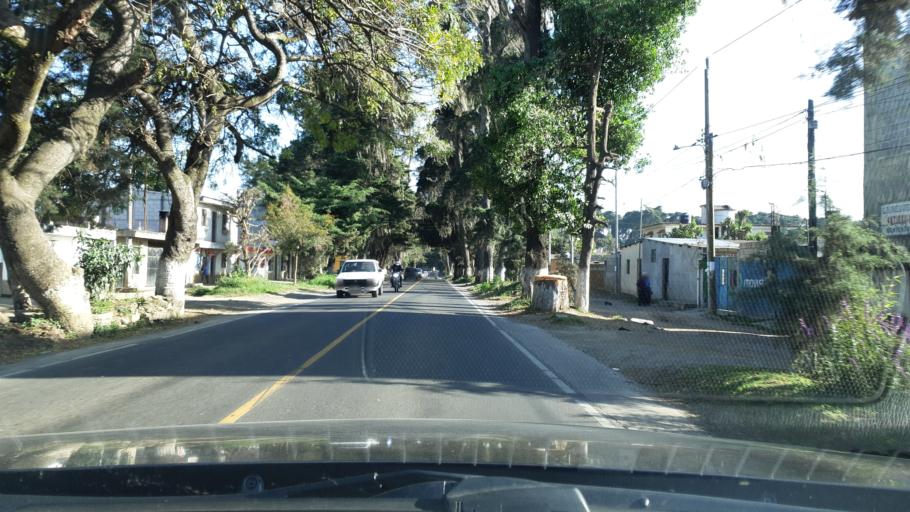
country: GT
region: Chimaltenango
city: El Tejar
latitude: 14.6439
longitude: -90.8105
